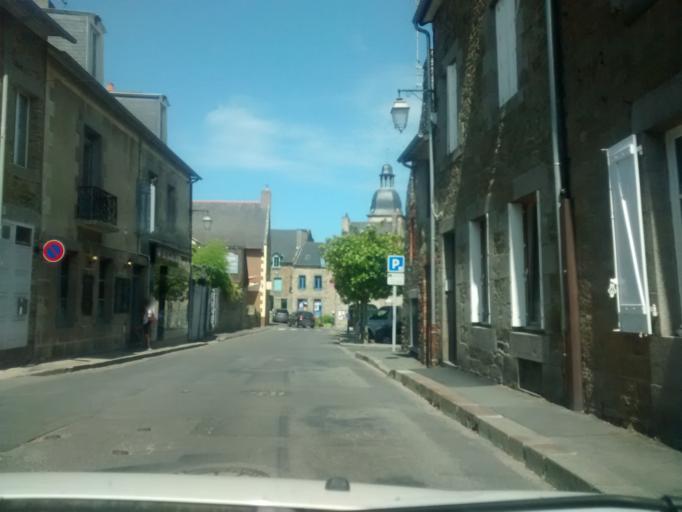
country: FR
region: Brittany
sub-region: Departement d'Ille-et-Vilaine
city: Cancale
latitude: 48.6763
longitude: -1.8508
